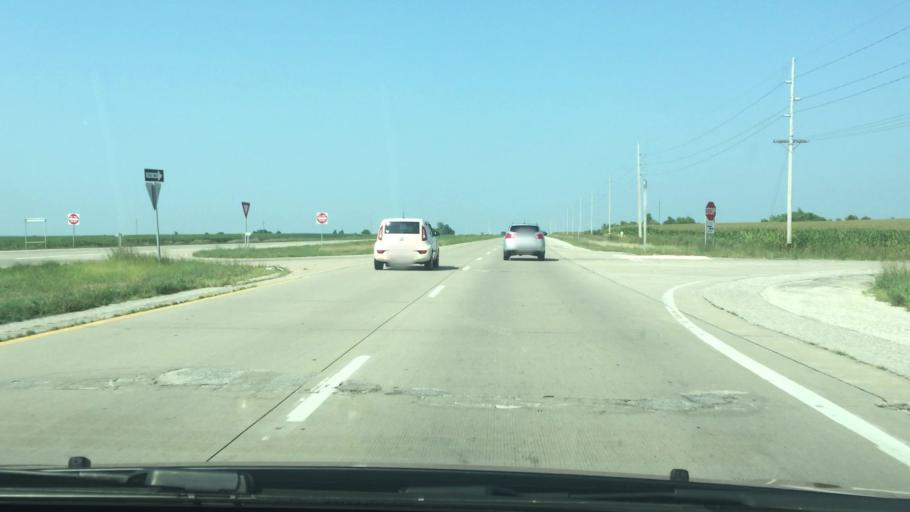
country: US
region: Iowa
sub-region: Muscatine County
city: Muscatine
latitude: 41.4789
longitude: -90.9950
